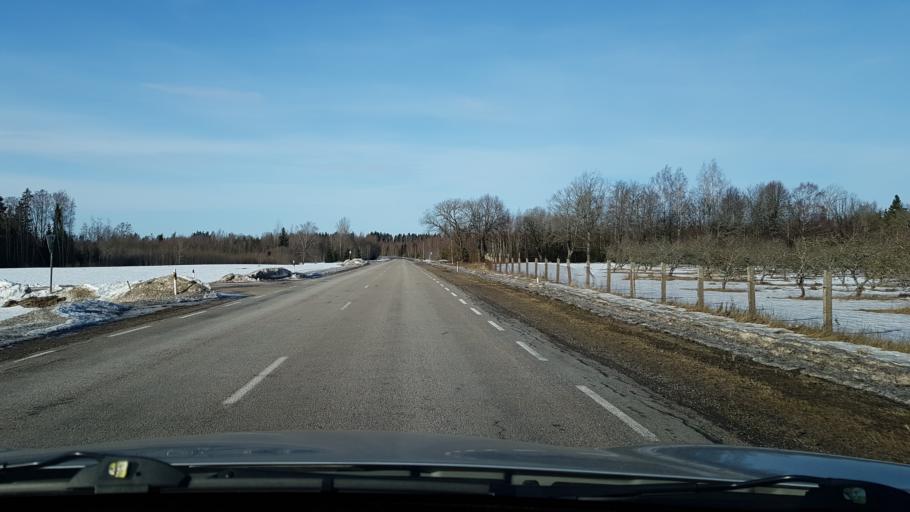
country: EE
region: Viljandimaa
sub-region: Suure-Jaani vald
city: Suure-Jaani
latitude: 58.5243
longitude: 25.5207
